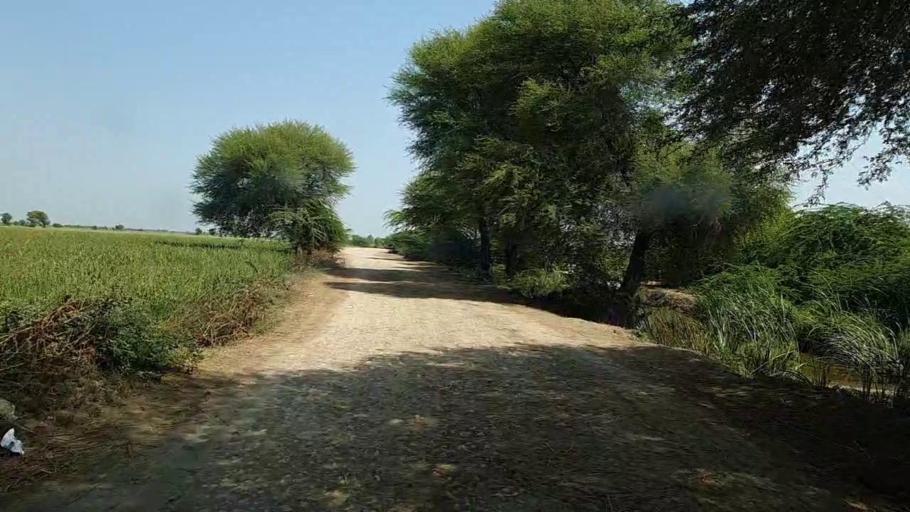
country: PK
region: Sindh
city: Kario
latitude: 24.6373
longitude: 68.4885
